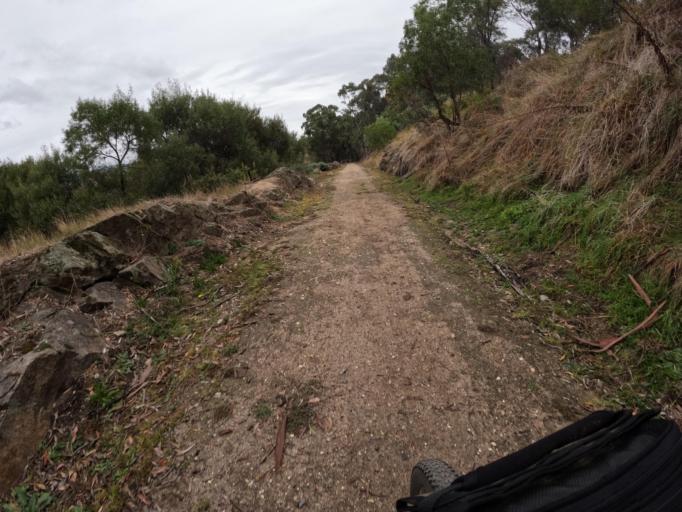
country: AU
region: New South Wales
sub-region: Greater Hume Shire
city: Holbrook
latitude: -36.1777
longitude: 147.3818
